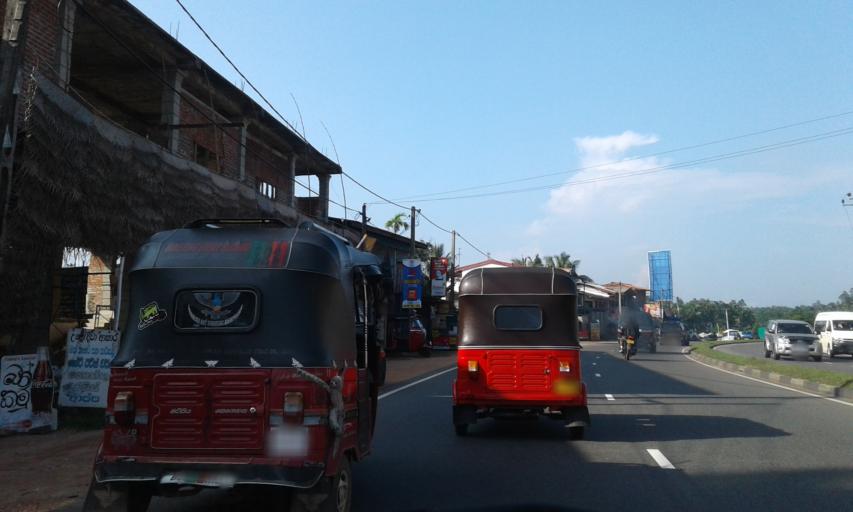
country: LK
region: Western
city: Gampaha
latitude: 7.0423
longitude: 79.9943
